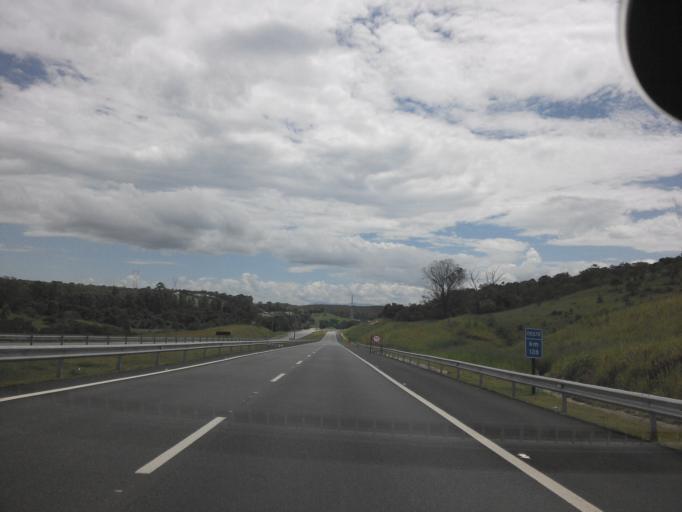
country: BR
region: Sao Paulo
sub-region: Taubate
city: Taubate
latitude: -23.1010
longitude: -45.6008
